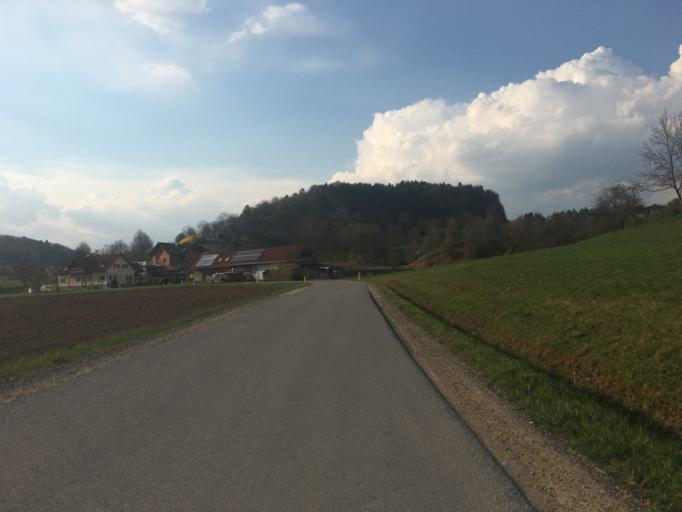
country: AT
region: Styria
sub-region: Politischer Bezirk Graz-Umgebung
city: Nestelbach bei Graz
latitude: 47.0832
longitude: 15.6252
